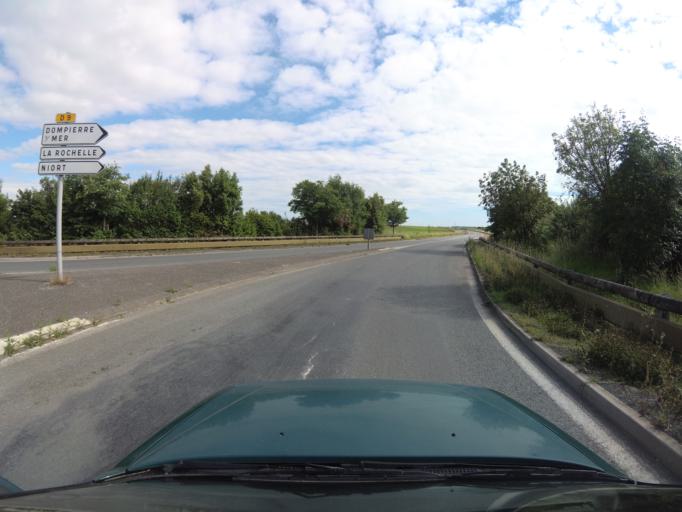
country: FR
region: Poitou-Charentes
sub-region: Departement de la Charente-Maritime
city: Saint-Xandre
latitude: 46.2169
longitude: -1.0900
